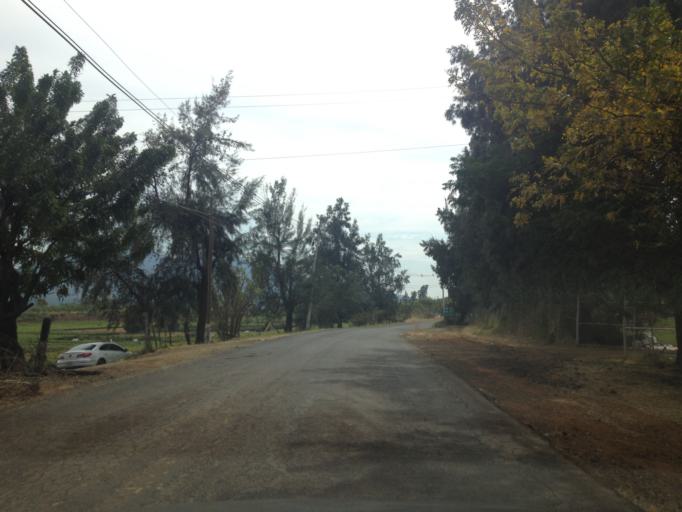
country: MX
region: Michoacan
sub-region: Ziracuaretiro
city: Patuan
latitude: 19.4265
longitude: -101.9235
